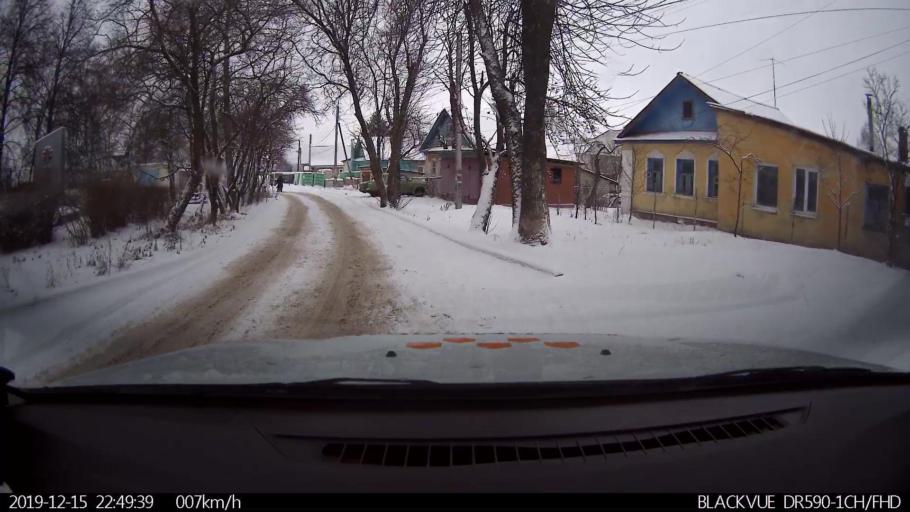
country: RU
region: Nizjnij Novgorod
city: Nizhniy Novgorod
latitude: 56.2339
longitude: 43.9785
